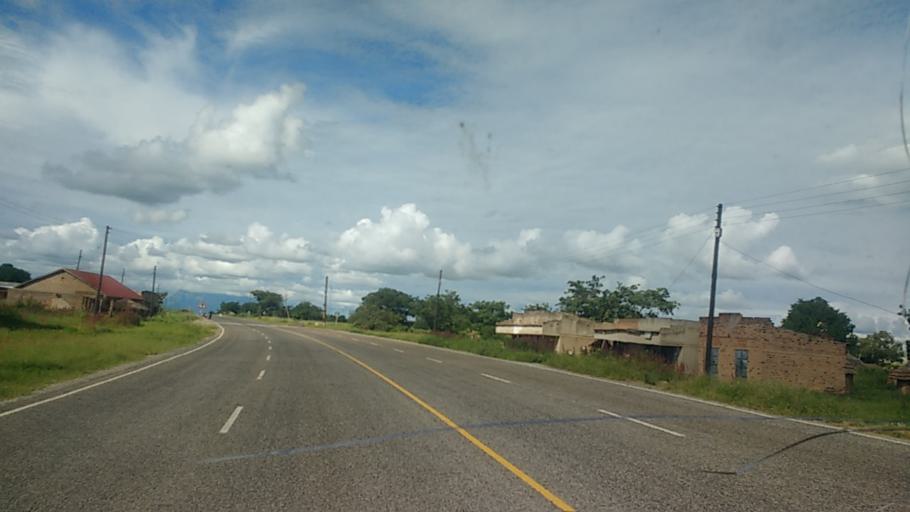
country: UG
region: Eastern Region
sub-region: Katakwi District
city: Katakwi
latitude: 1.9123
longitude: 34.0373
